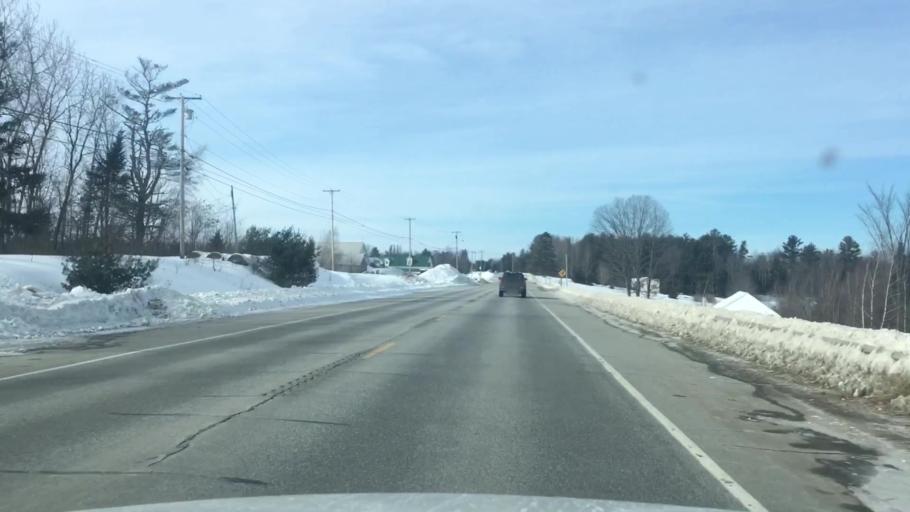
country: US
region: Maine
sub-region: Penobscot County
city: Kenduskeag
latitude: 44.9507
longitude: -68.9478
